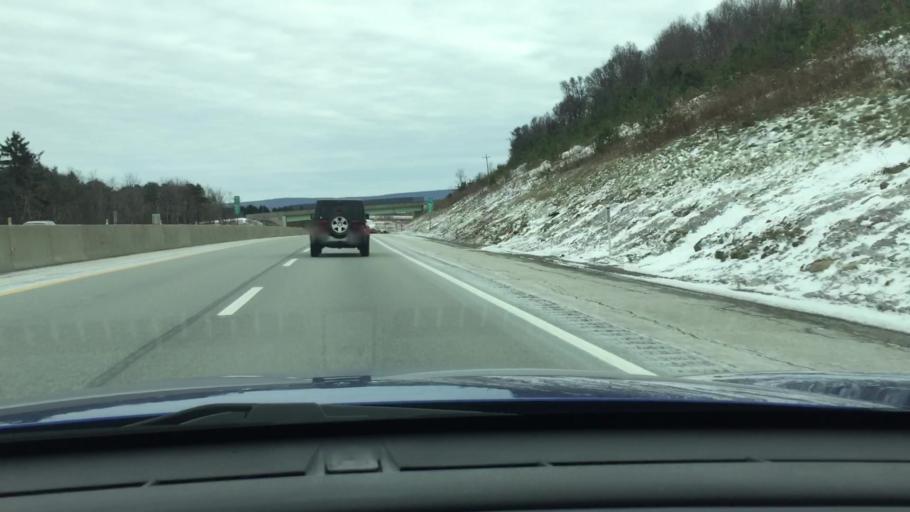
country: US
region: Pennsylvania
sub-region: Somerset County
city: Berlin
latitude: 39.9860
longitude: -78.9611
